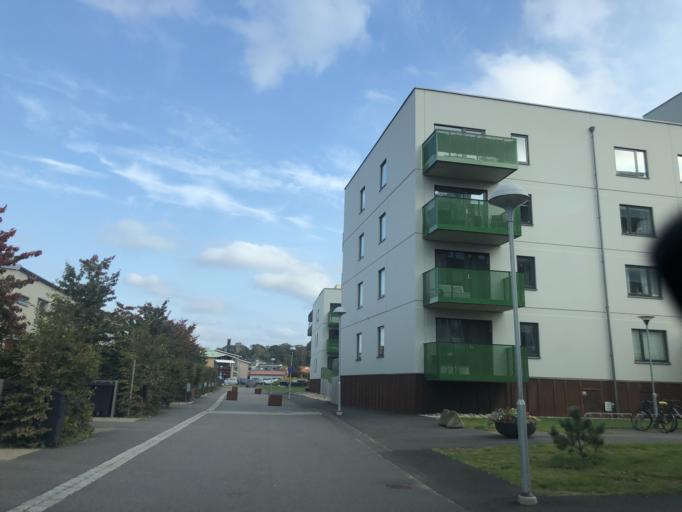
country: SE
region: Vaestra Goetaland
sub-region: Molndal
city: Moelndal
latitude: 57.6524
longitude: 11.9995
